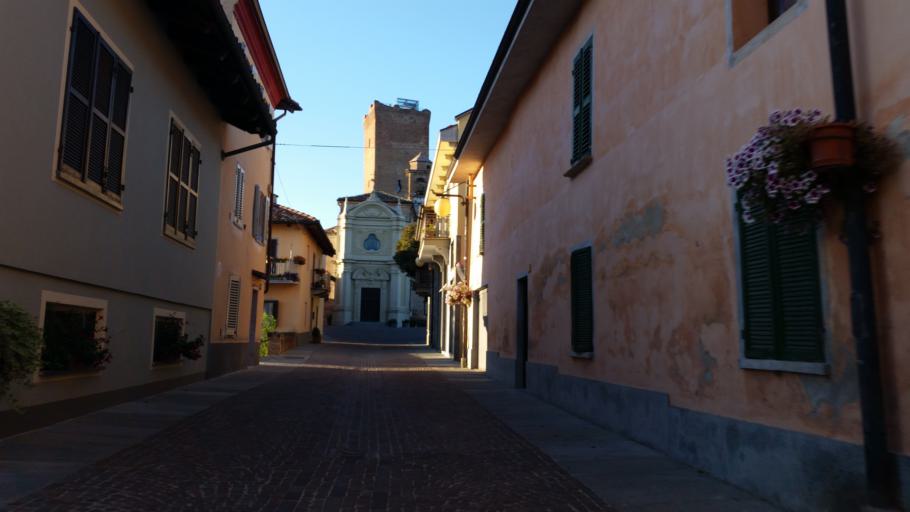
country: IT
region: Piedmont
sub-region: Provincia di Cuneo
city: Barbaresco
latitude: 44.7264
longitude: 8.0805
